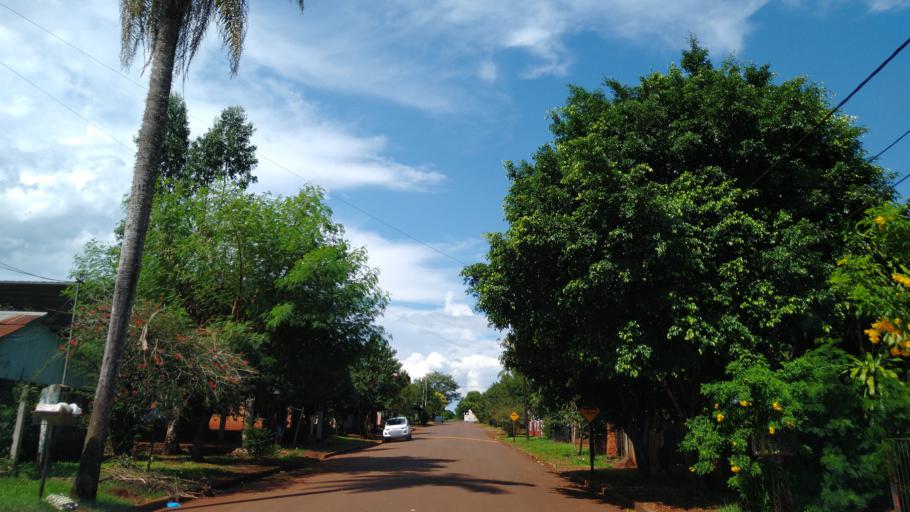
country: AR
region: Misiones
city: Puerto Libertad
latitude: -25.9689
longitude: -54.5741
